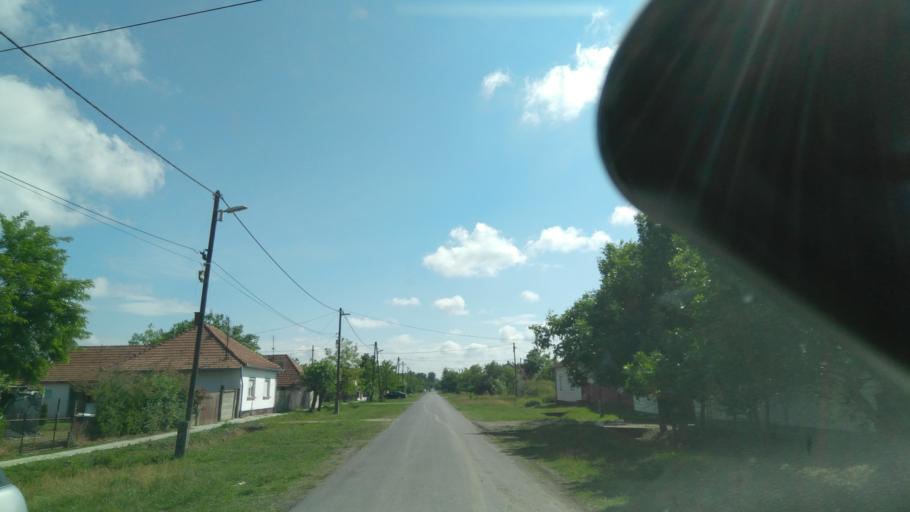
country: HU
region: Bekes
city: Bekes
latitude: 46.7730
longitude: 21.1100
